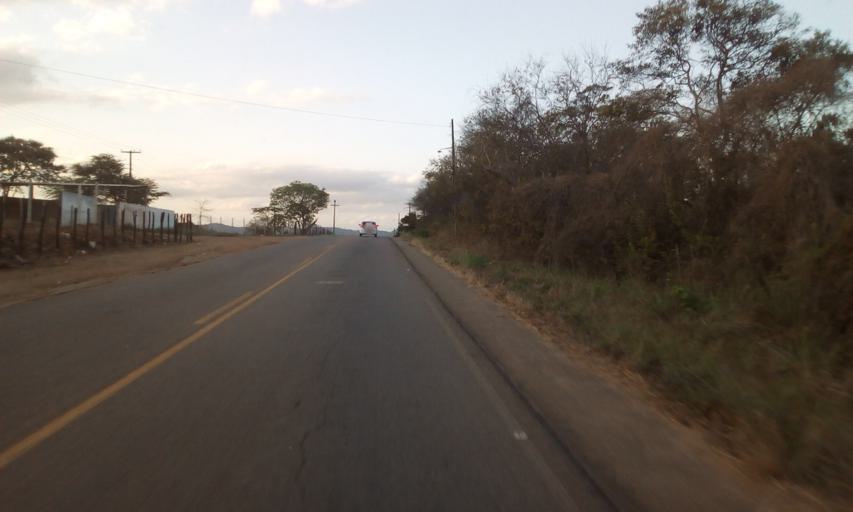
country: BR
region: Paraiba
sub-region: Guarabira
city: Guarabira
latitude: -6.8930
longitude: -35.4646
